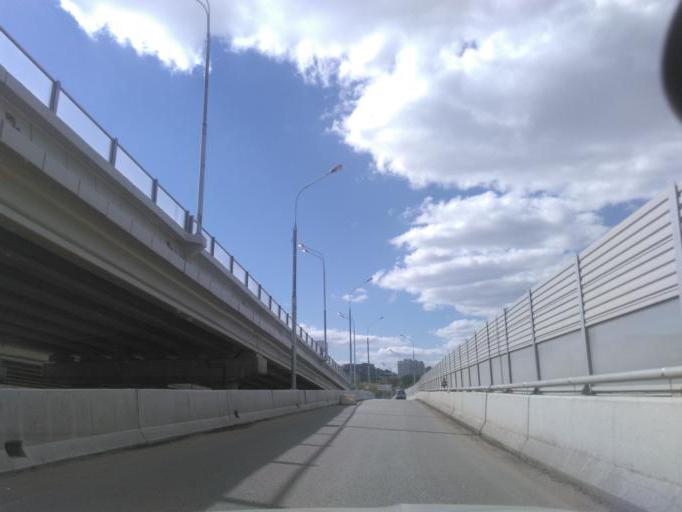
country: RU
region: Moscow
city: Novokhovrino
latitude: 55.8666
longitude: 37.5119
